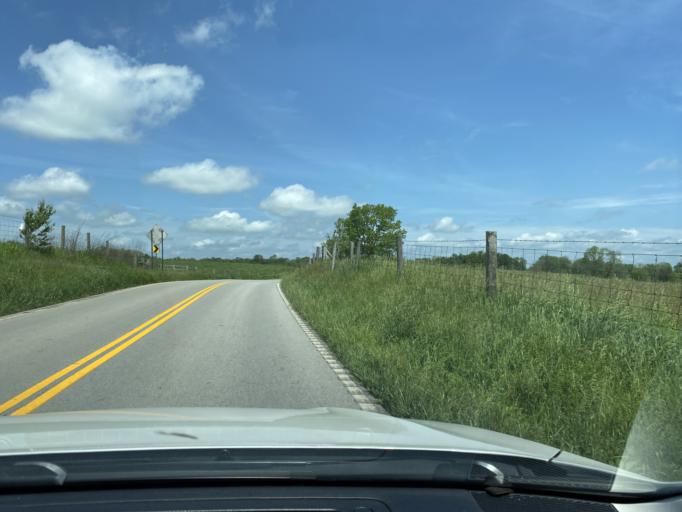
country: US
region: Kentucky
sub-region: Scott County
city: Georgetown
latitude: 38.2458
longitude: -84.5863
